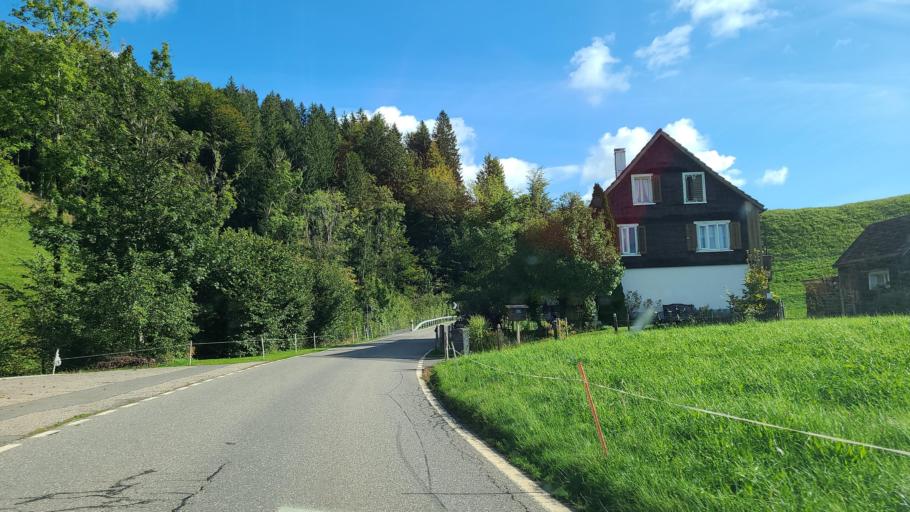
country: CH
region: Schwyz
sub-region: Bezirk Einsiedeln
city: Einsiedeln
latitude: 47.1336
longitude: 8.8006
